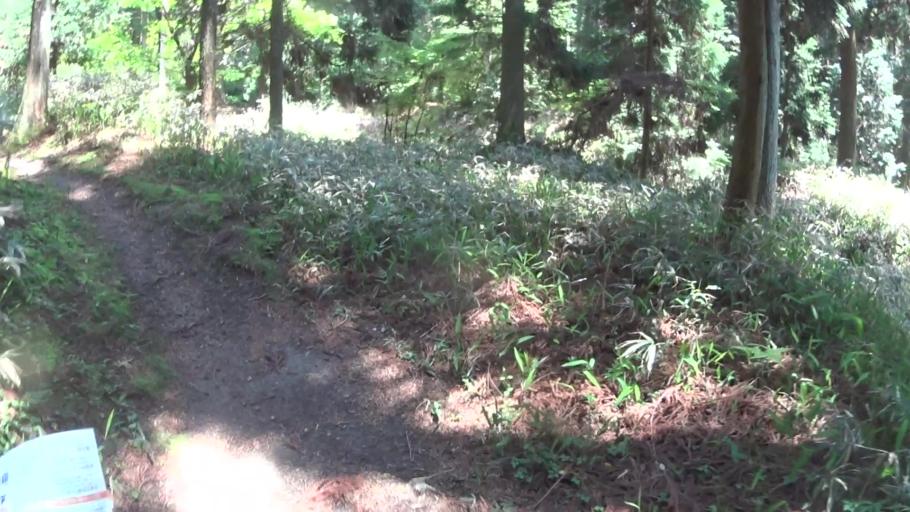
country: JP
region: Shiga Prefecture
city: Otsu-shi
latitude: 35.0759
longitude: 135.8345
